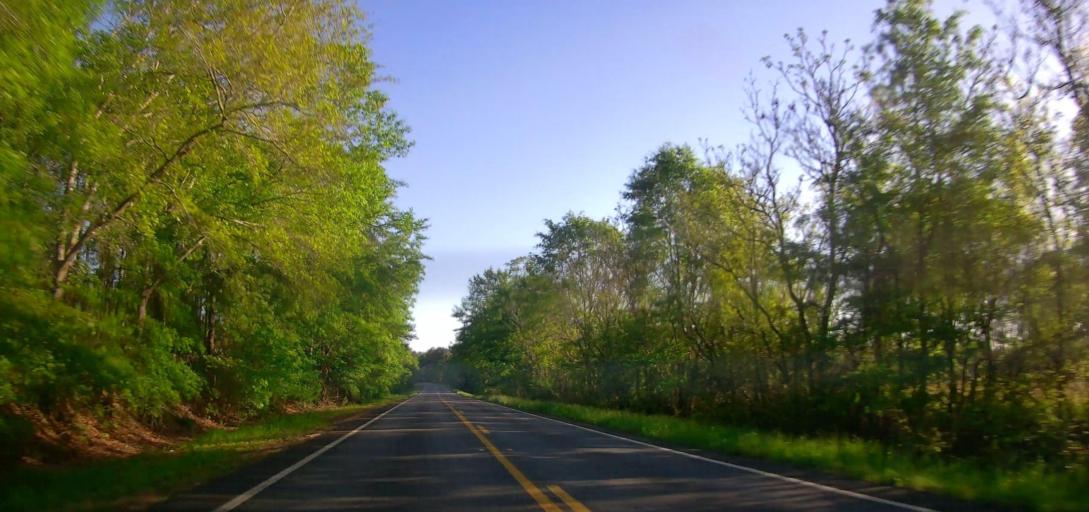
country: US
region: Georgia
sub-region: Macon County
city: Oglethorpe
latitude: 32.2892
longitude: -84.1567
